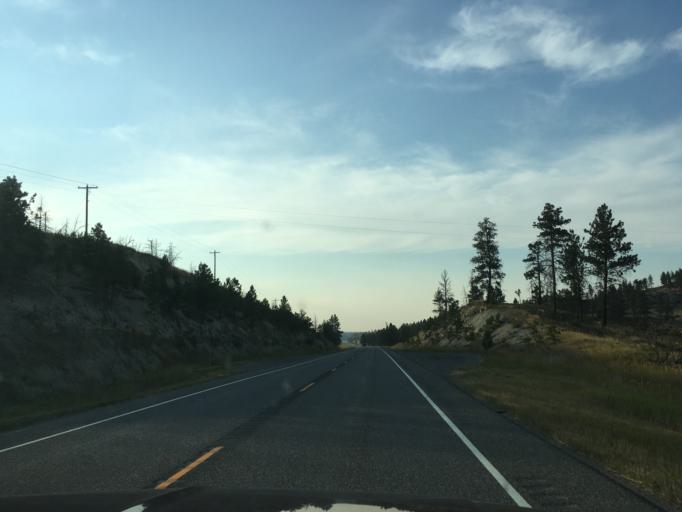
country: US
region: Montana
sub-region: Musselshell County
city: Roundup
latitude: 46.2764
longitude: -108.4742
